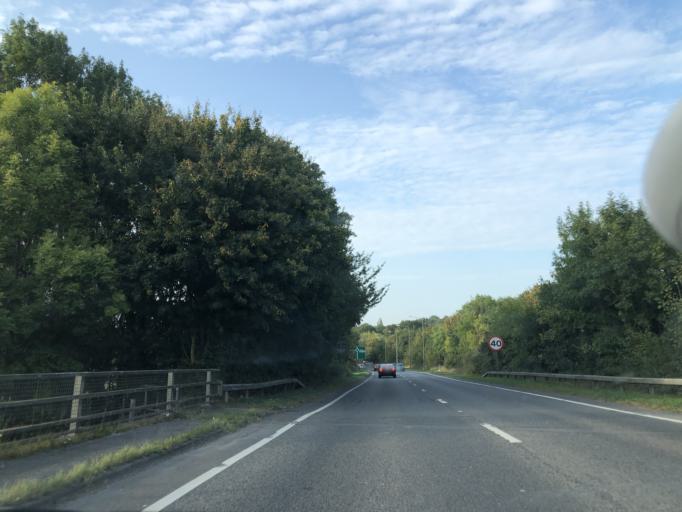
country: GB
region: England
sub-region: East Sussex
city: Robertsbridge
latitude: 50.9888
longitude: 0.4796
